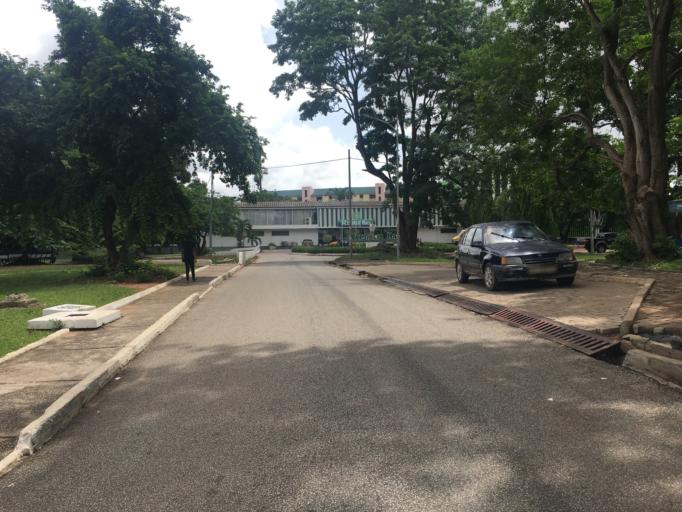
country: GH
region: Ashanti
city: Kumasi
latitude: 6.6770
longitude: -1.5739
